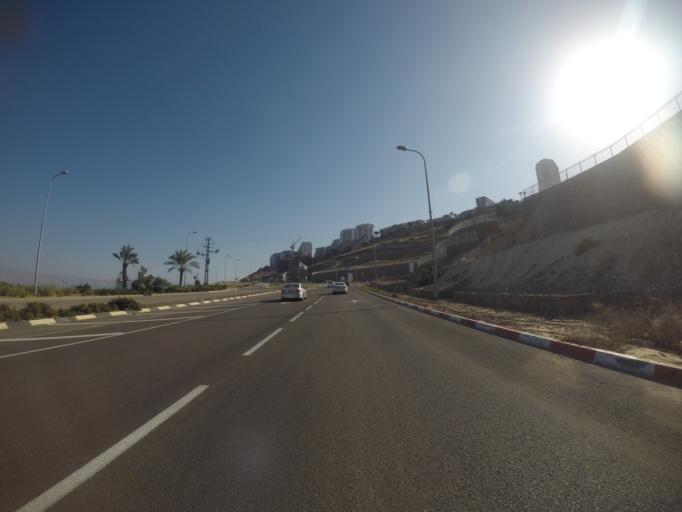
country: IL
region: Northern District
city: Tiberias
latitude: 32.8015
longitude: 35.5315
